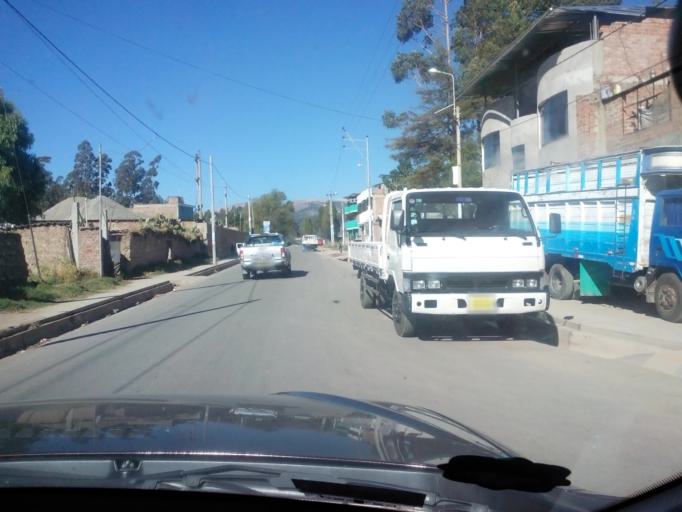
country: PE
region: Apurimac
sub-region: Provincia de Andahuaylas
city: Talavera
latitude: -13.6589
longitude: -73.4276
